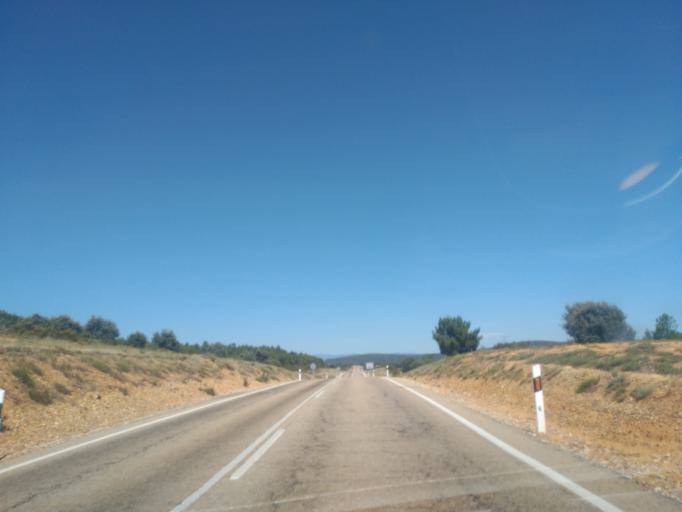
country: ES
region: Castille and Leon
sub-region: Provincia de Zamora
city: Ferreras de Abajo
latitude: 41.8842
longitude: -6.0236
